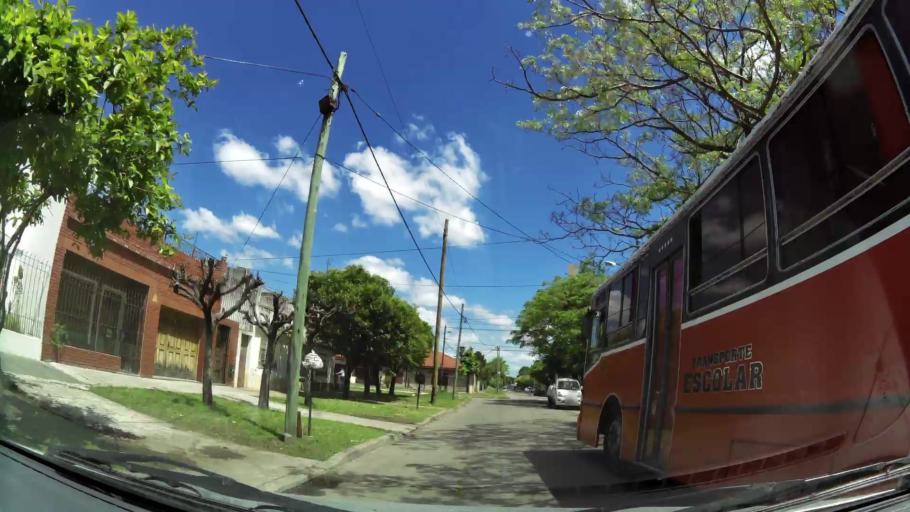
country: AR
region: Buenos Aires
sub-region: Partido de Lomas de Zamora
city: Lomas de Zamora
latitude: -34.7347
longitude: -58.4145
